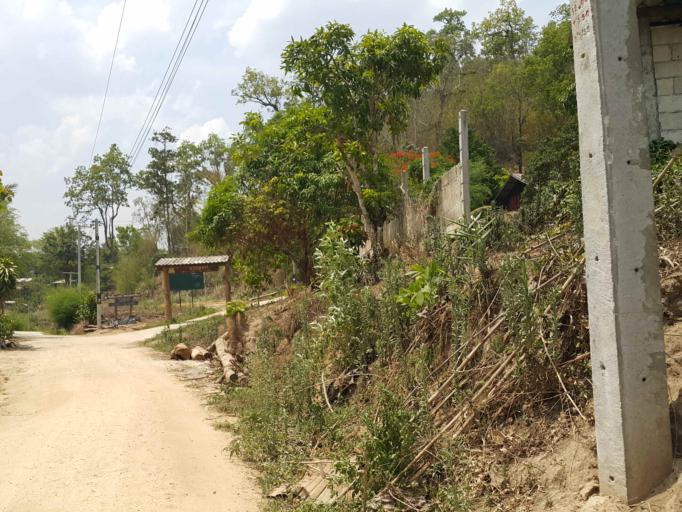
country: TH
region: Chiang Mai
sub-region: Amphoe Chiang Dao
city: Chiang Dao
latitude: 19.2703
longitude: 98.7677
